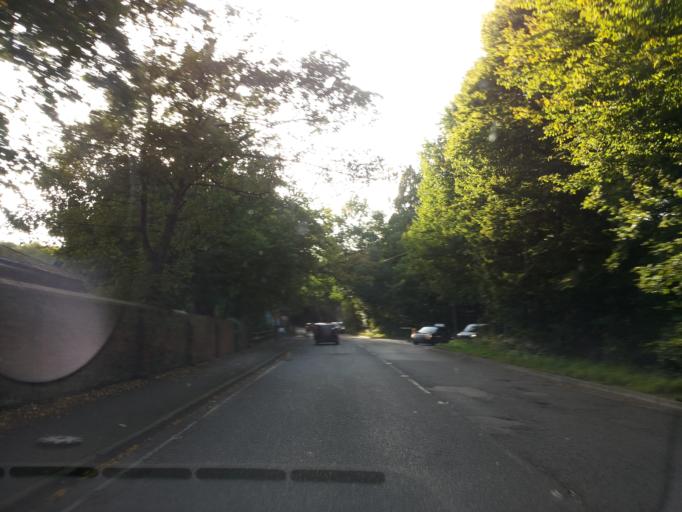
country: GB
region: England
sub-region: Surrey
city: Chertsey
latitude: 51.3803
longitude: -0.5209
